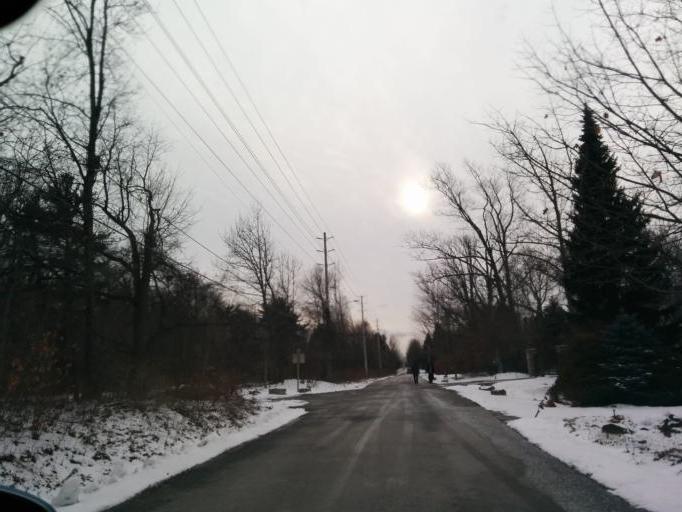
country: CA
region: Ontario
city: Mississauga
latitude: 43.5444
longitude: -79.6411
